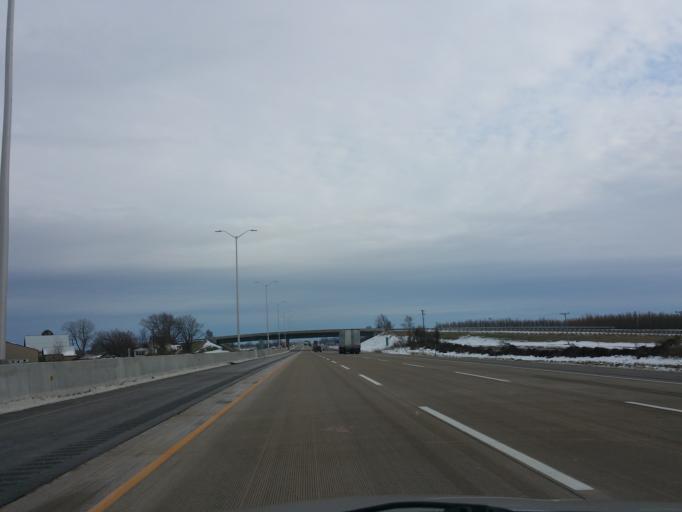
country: US
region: Illinois
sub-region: McHenry County
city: Marengo
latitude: 42.1958
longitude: -88.6704
